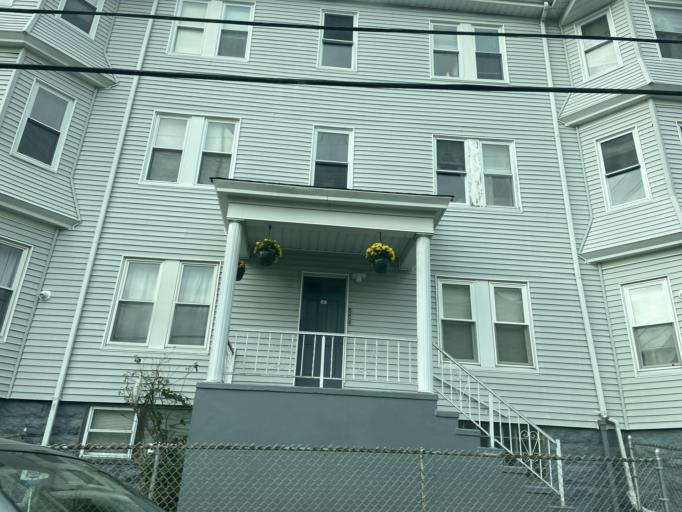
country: US
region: Massachusetts
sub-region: Bristol County
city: Fall River
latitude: 41.6979
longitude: -71.1418
